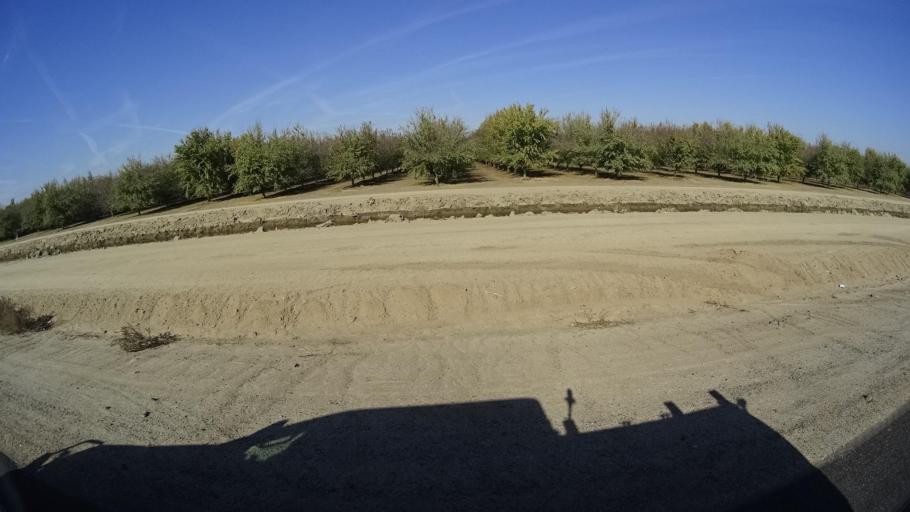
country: US
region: California
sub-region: Kern County
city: Wasco
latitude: 35.6453
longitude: -119.3106
